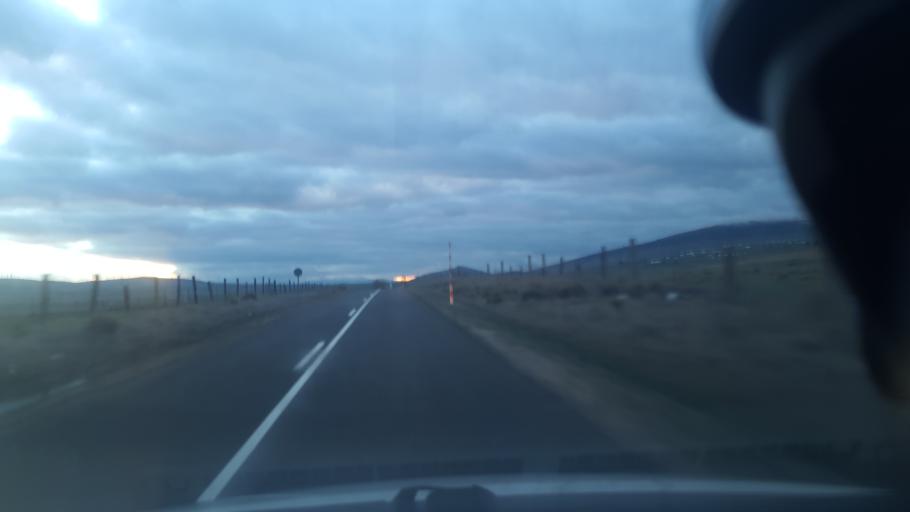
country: ES
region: Castille and Leon
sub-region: Provincia de Segovia
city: Villacastin
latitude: 40.6978
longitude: -4.3916
